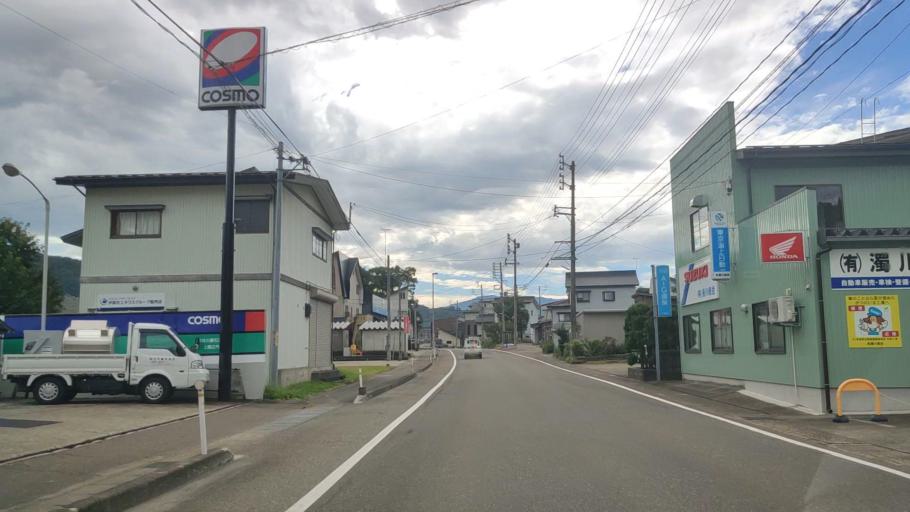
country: JP
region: Niigata
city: Arai
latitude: 36.9905
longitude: 138.2705
